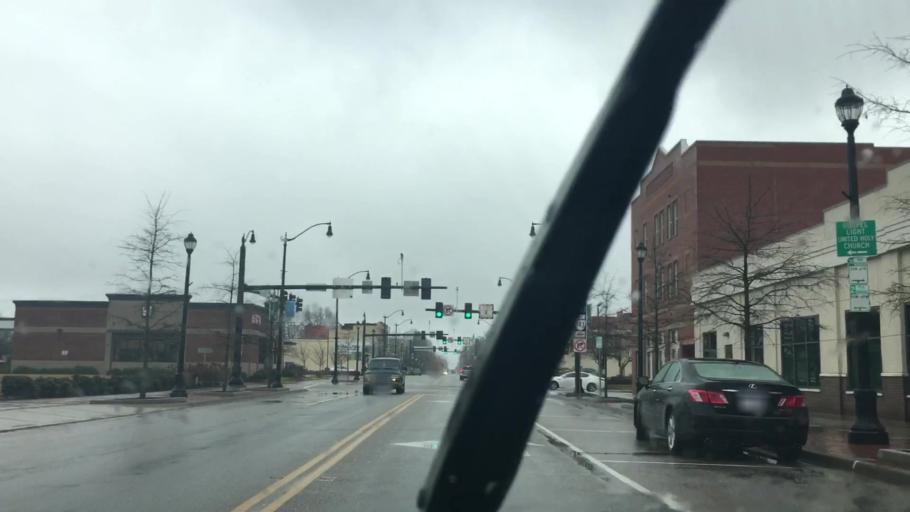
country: US
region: Virginia
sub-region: City of Newport News
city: Newport News
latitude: 36.9832
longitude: -76.4222
